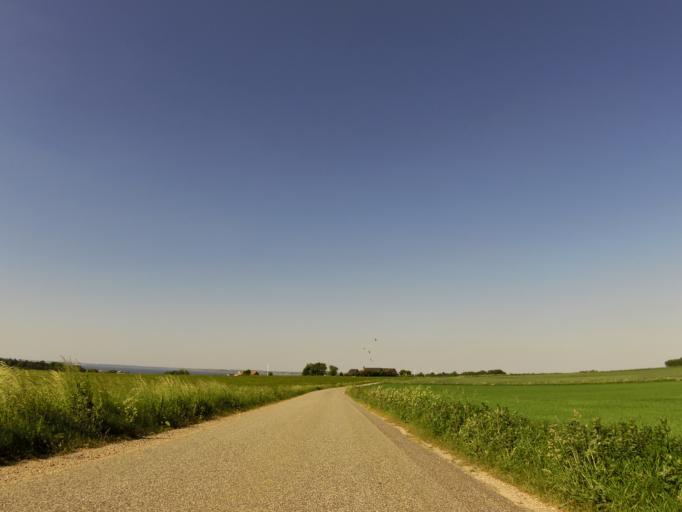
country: DK
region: Central Jutland
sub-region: Holstebro Kommune
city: Vinderup
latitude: 56.4585
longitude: 8.6967
